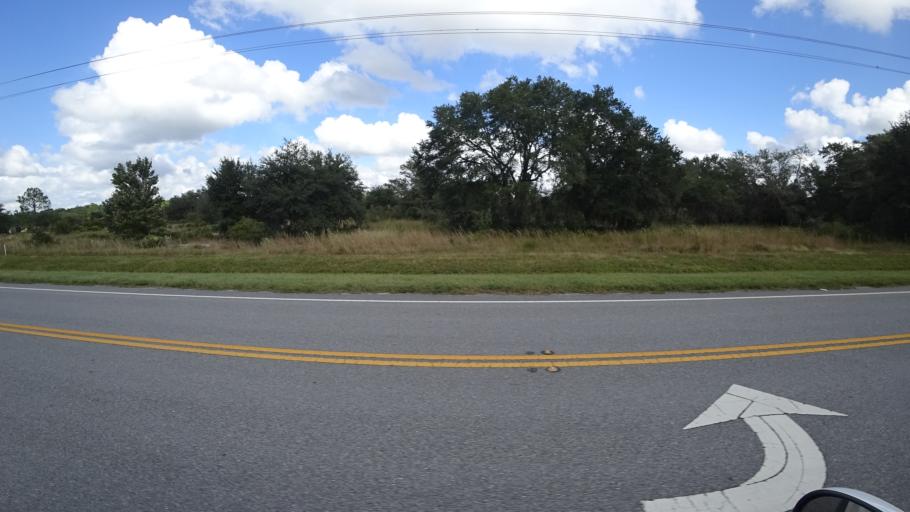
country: US
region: Florida
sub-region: Hillsborough County
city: Wimauma
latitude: 27.4599
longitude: -82.1225
